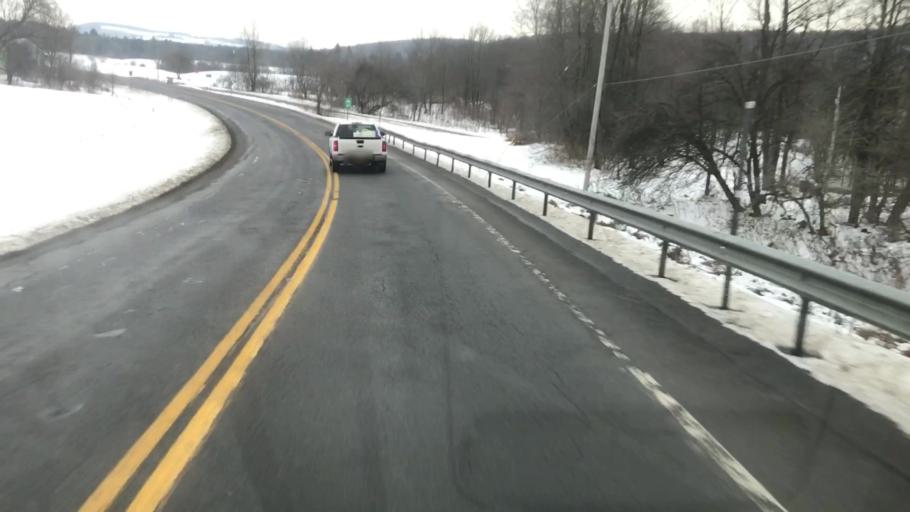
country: US
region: New York
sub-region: Tompkins County
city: Groton
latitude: 42.6828
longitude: -76.3011
